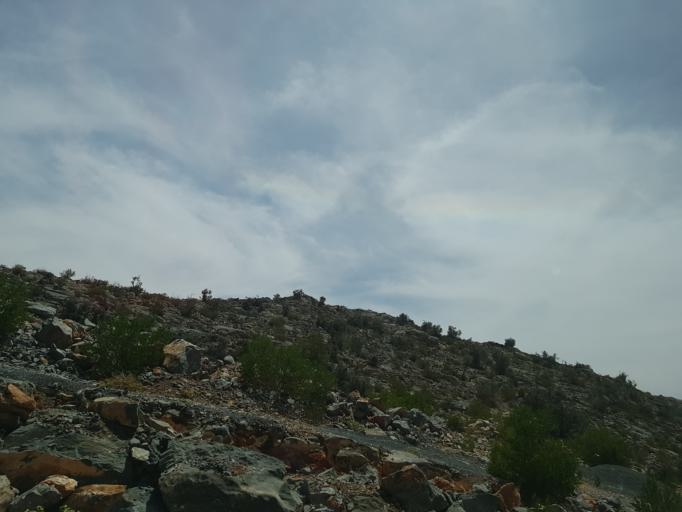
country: OM
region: Al Batinah
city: Bayt al `Awabi
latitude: 23.1381
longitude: 57.5435
